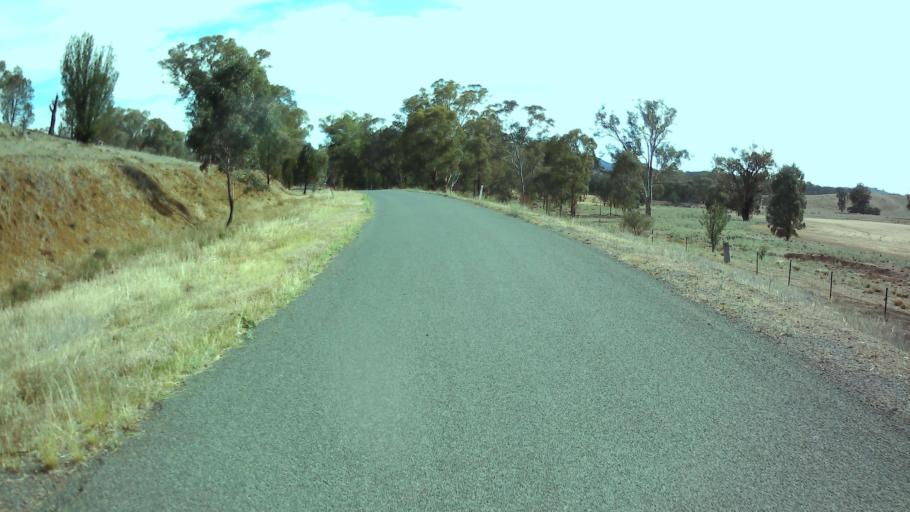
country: AU
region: New South Wales
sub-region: Weddin
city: Grenfell
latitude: -33.8176
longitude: 148.2914
